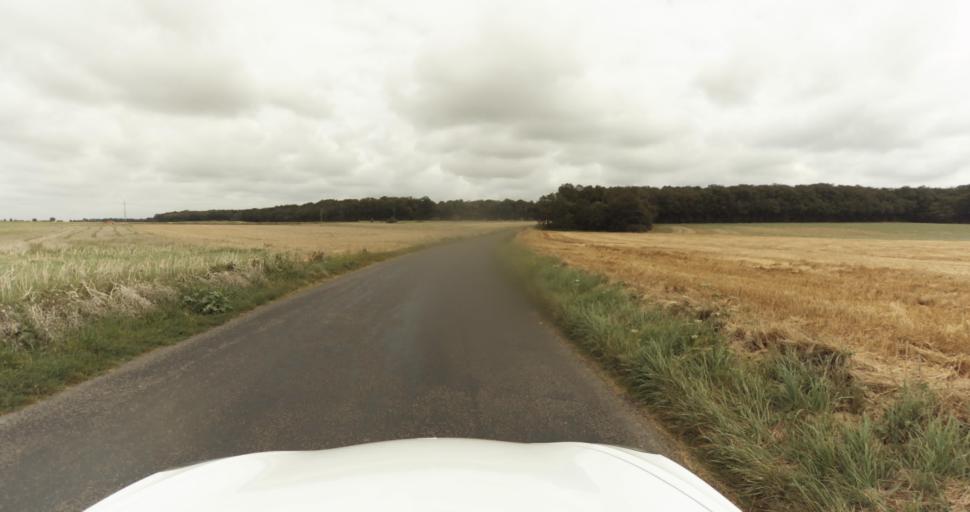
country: FR
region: Haute-Normandie
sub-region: Departement de l'Eure
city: Claville
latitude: 49.0319
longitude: 1.0532
